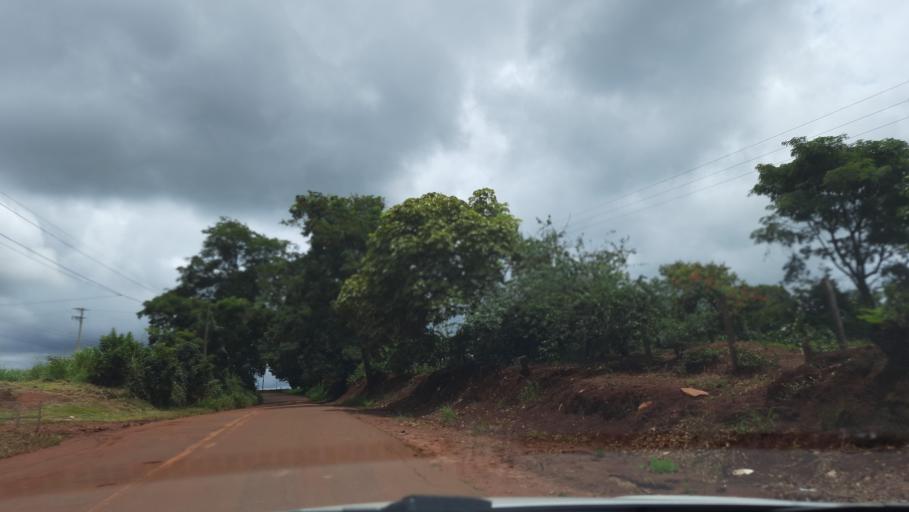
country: BR
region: Sao Paulo
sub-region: Casa Branca
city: Casa Branca
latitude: -21.7910
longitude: -47.0983
